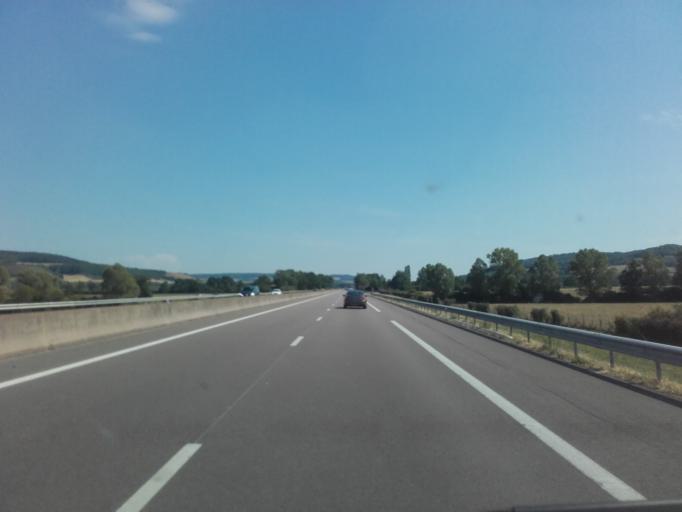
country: FR
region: Bourgogne
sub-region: Departement de la Cote-d'Or
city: Vitteaux
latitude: 47.3412
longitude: 4.4665
